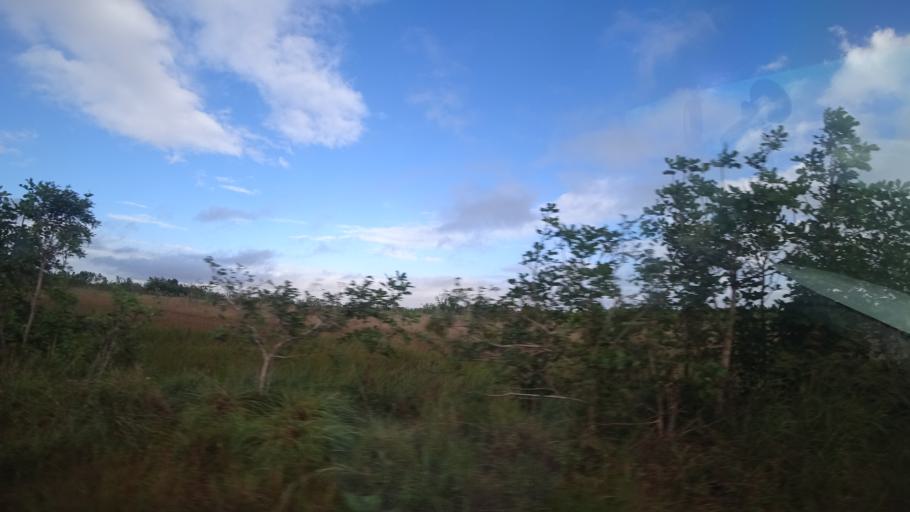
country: MZ
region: Sofala
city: Beira
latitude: -19.6392
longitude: 35.0593
